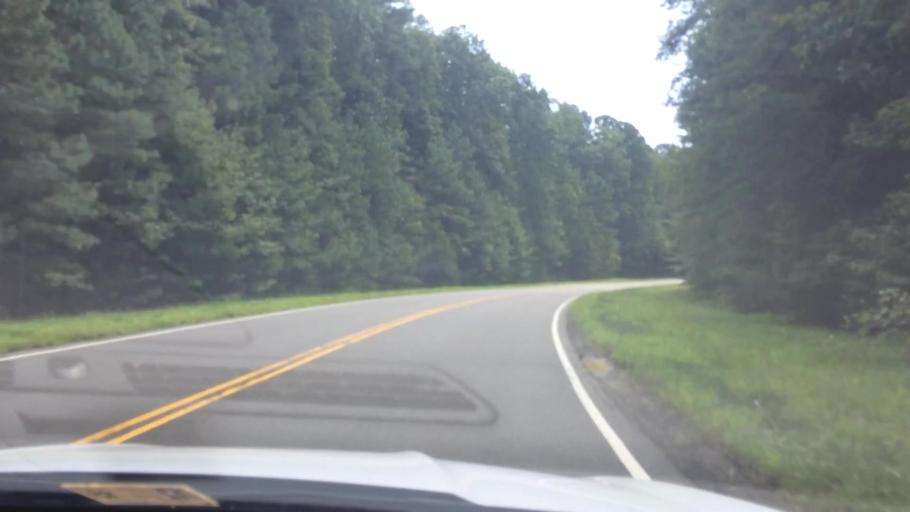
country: US
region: Virginia
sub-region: James City County
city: Williamsburg
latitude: 37.2956
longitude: -76.7354
